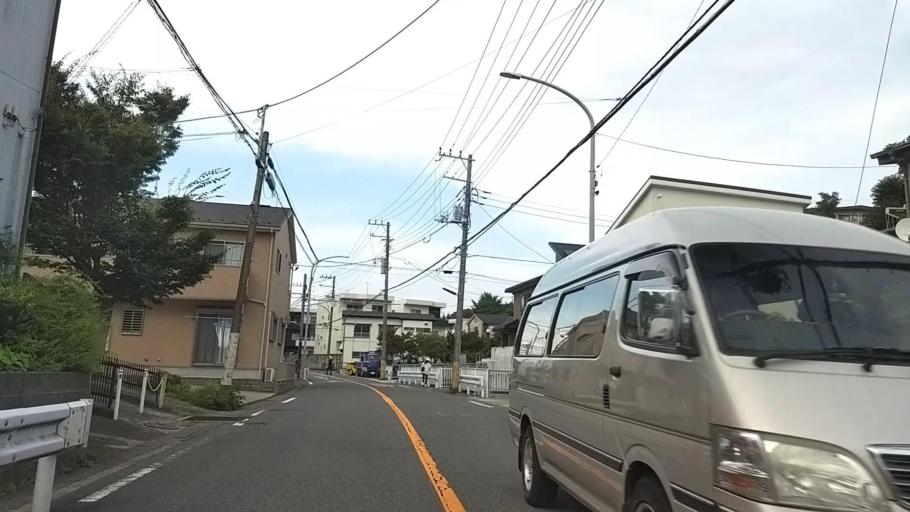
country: JP
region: Kanagawa
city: Yokohama
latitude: 35.4820
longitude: 139.5708
